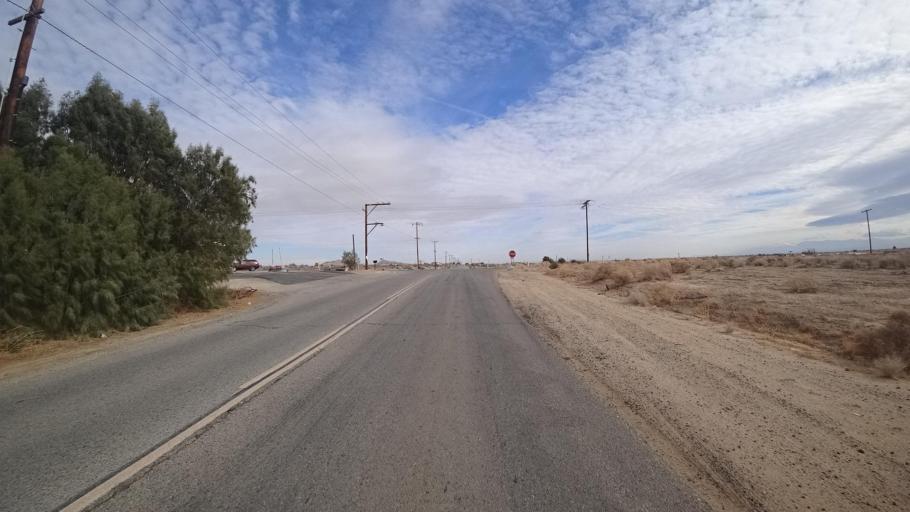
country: US
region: California
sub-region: Kern County
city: Rosamond
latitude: 34.8636
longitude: -118.2919
